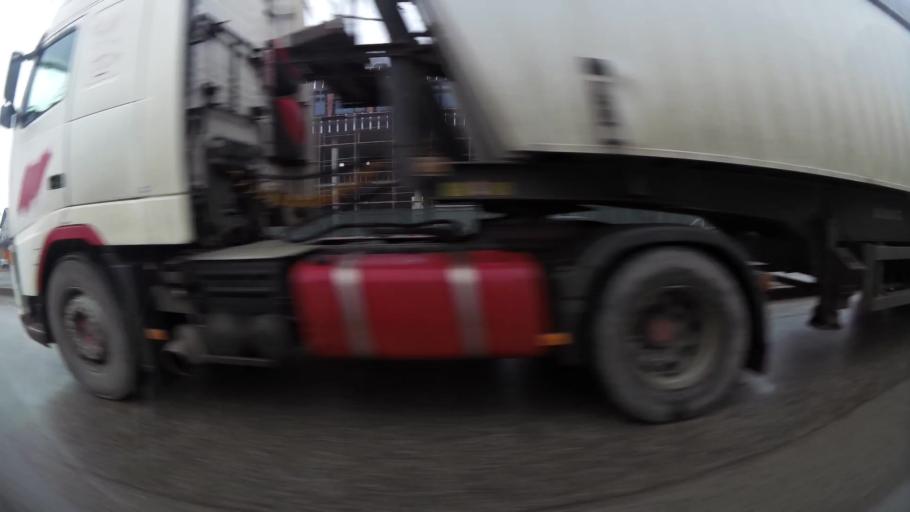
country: BG
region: Sofia-Capital
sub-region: Stolichna Obshtina
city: Sofia
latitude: 42.7095
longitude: 23.4211
